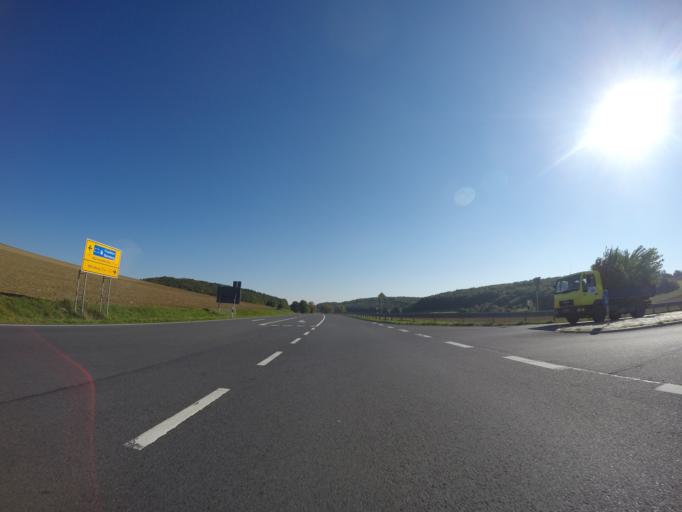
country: DE
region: Bavaria
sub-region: Regierungsbezirk Unterfranken
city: Waldbrunn
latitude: 49.7743
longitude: 9.7847
